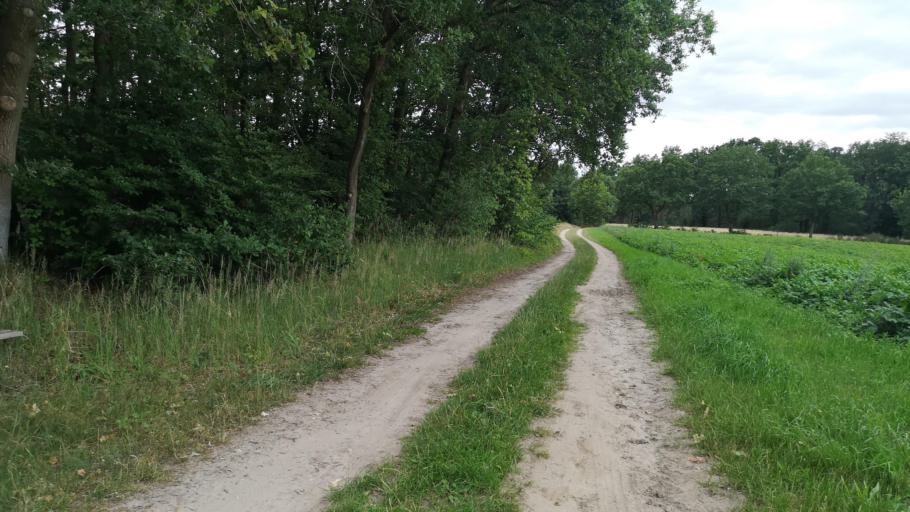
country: DE
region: Lower Saxony
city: Thomasburg
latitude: 53.2100
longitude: 10.6956
